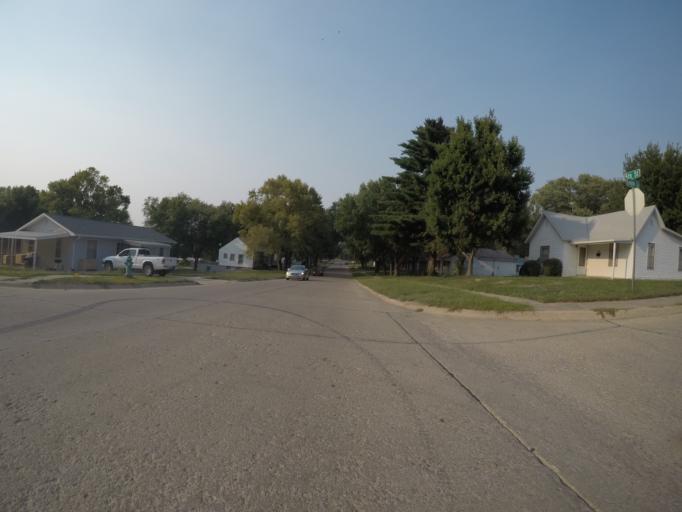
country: US
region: Nebraska
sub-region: Gage County
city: Beatrice
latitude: 40.2745
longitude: -96.7480
